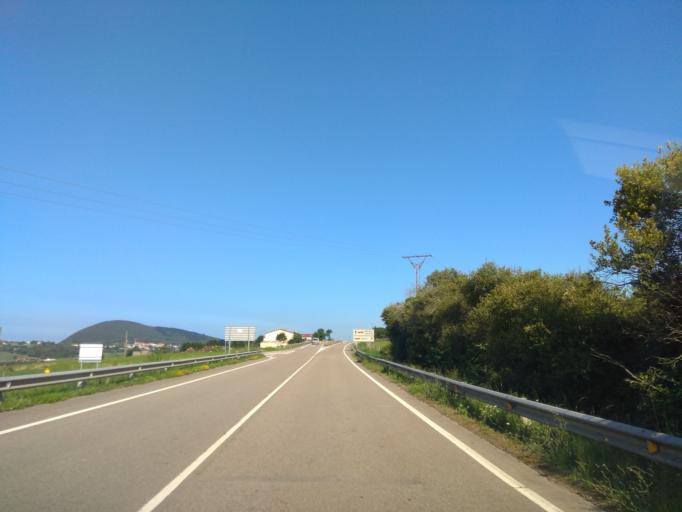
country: ES
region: Cantabria
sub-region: Provincia de Cantabria
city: Bareyo
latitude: 43.4744
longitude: -3.5987
